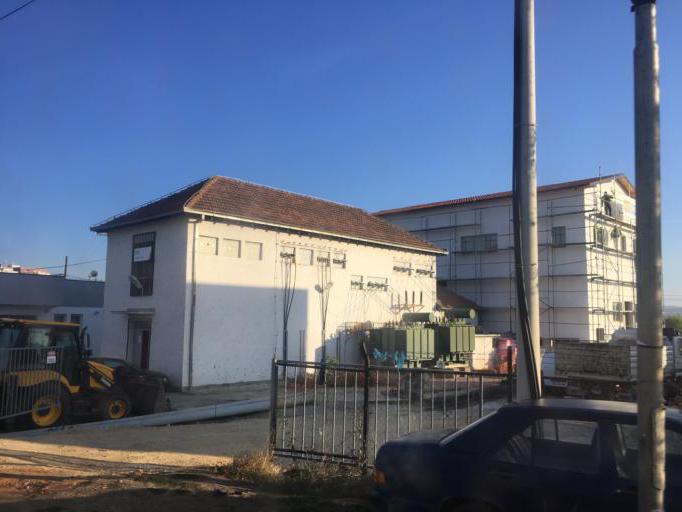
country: XK
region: Pristina
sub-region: Komuna e Drenasit
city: Glogovac
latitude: 42.6185
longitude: 20.8969
